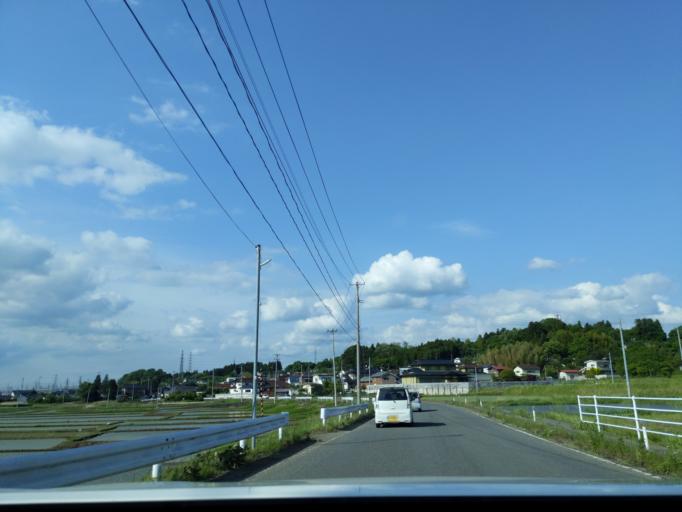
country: JP
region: Fukushima
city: Koriyama
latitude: 37.3727
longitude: 140.4100
